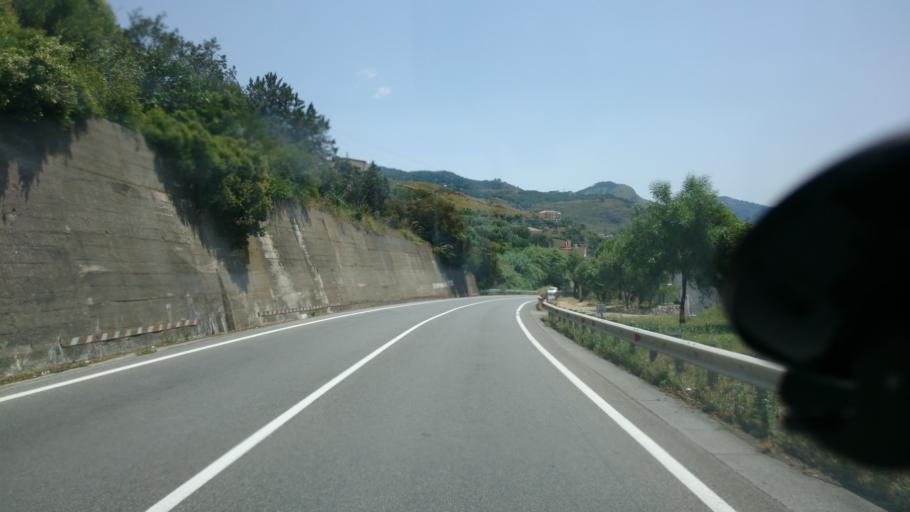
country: IT
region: Calabria
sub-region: Provincia di Cosenza
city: Cittadella del Capo
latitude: 39.5388
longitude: 15.9047
